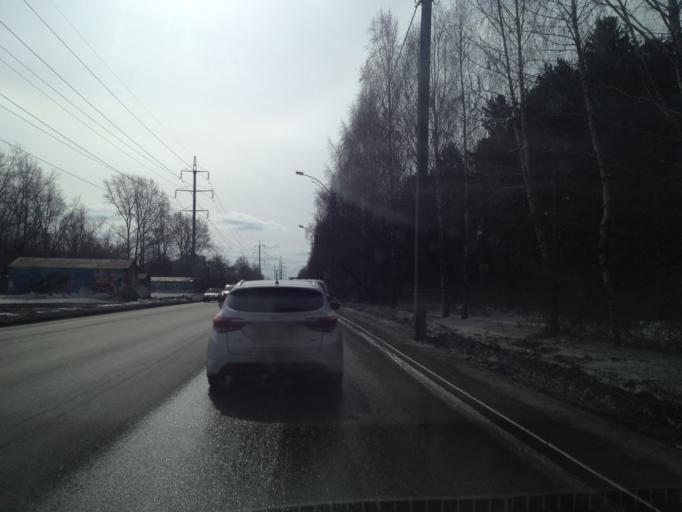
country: RU
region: Sverdlovsk
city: Sovkhoznyy
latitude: 56.7820
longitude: 60.5995
